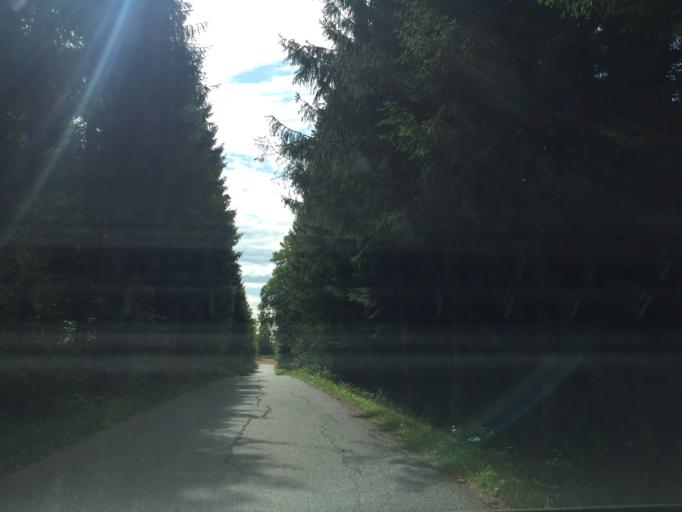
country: NO
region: Akershus
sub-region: Ski
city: Ski
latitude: 59.6529
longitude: 10.8721
